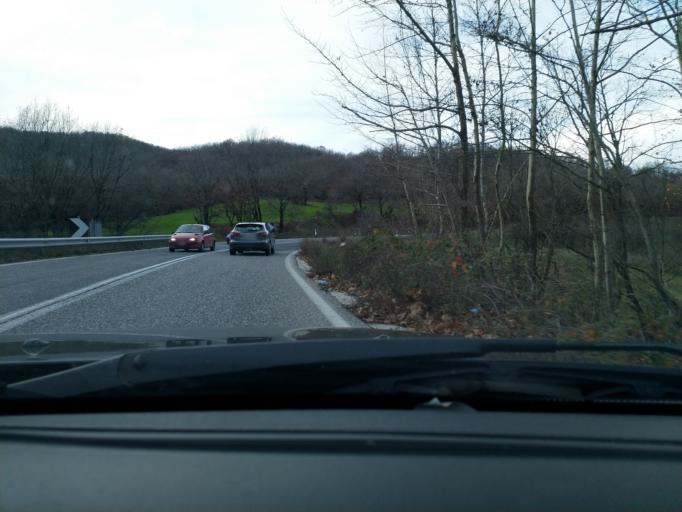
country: GR
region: Thessaly
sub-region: Trikala
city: Kastraki
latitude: 39.7422
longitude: 21.5372
